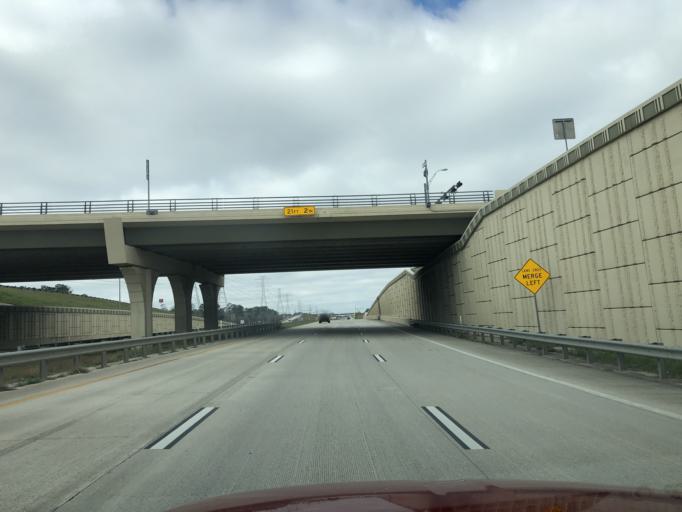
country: US
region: Texas
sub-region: Harris County
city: Spring
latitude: 30.0878
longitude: -95.4502
